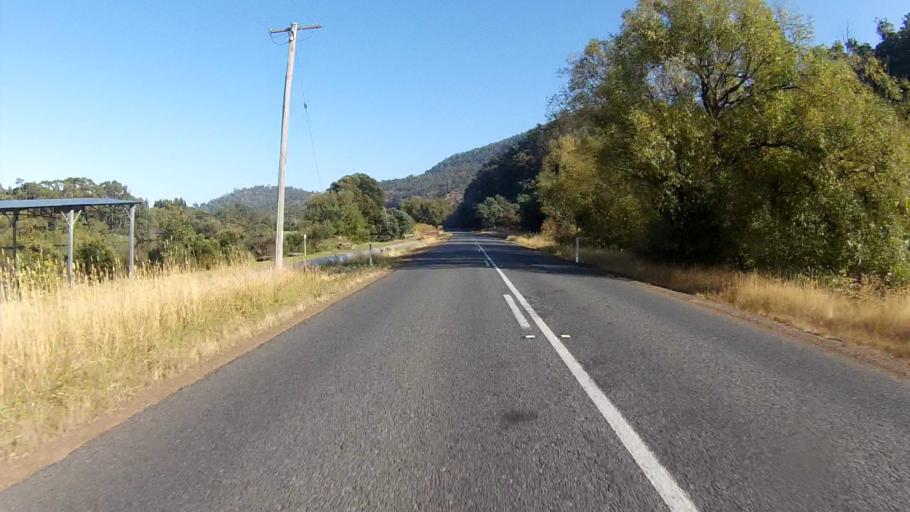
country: AU
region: Tasmania
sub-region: Derwent Valley
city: New Norfolk
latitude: -42.7753
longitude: 147.0809
